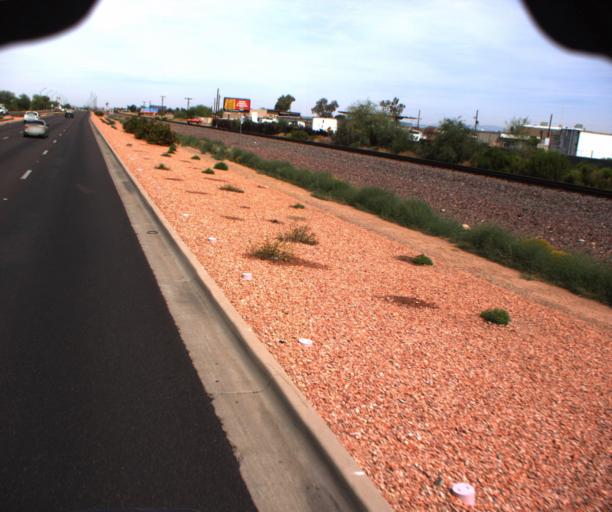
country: US
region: Arizona
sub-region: Maricopa County
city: Peoria
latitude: 33.5690
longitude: -112.2227
